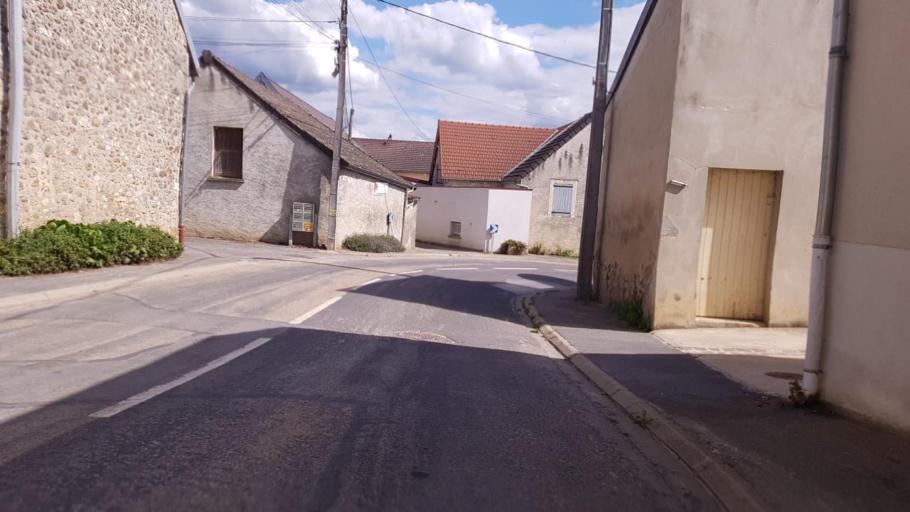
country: FR
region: Champagne-Ardenne
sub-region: Departement de la Marne
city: Dormans
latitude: 49.0667
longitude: 3.5929
